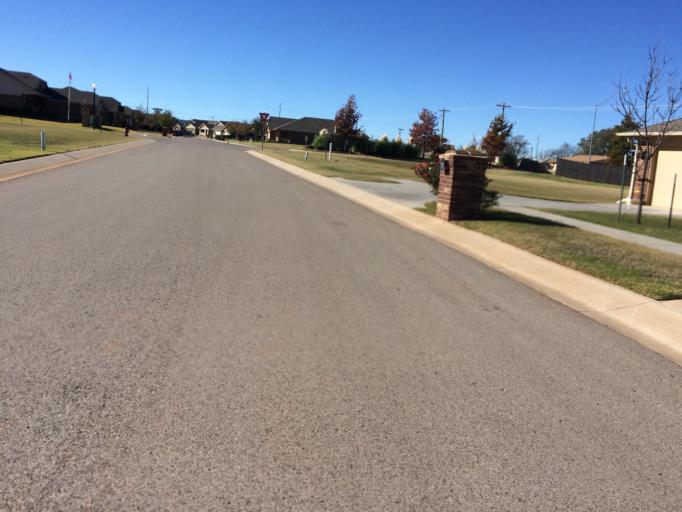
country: US
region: Oklahoma
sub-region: Cleveland County
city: Norman
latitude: 35.2612
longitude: -97.4546
